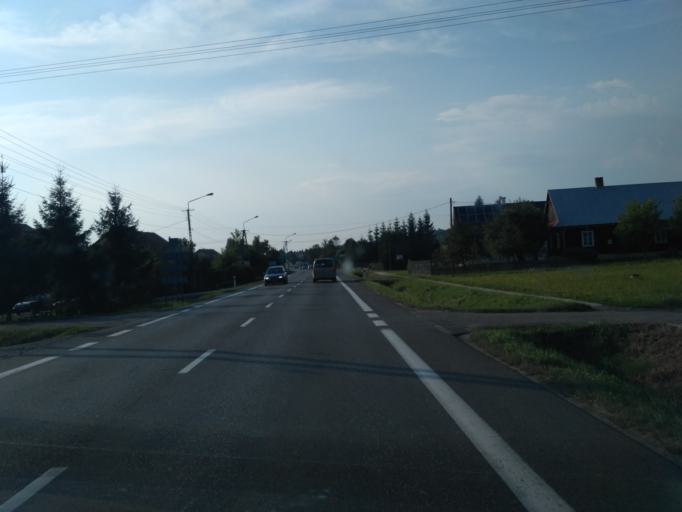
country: PL
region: Subcarpathian Voivodeship
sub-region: Powiat brzozowski
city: Stara Wies
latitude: 49.7319
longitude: 21.9992
